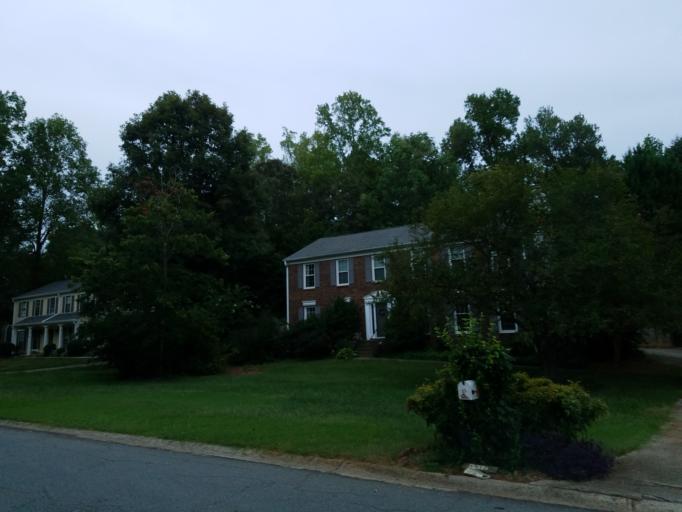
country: US
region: Georgia
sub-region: Fulton County
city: Sandy Springs
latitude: 33.9709
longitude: -84.4197
